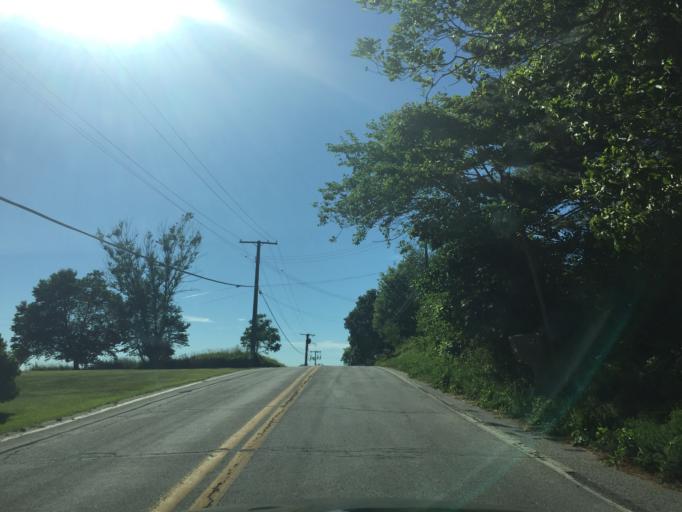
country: US
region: Maryland
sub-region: Carroll County
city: Westminster
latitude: 39.6001
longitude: -76.9407
